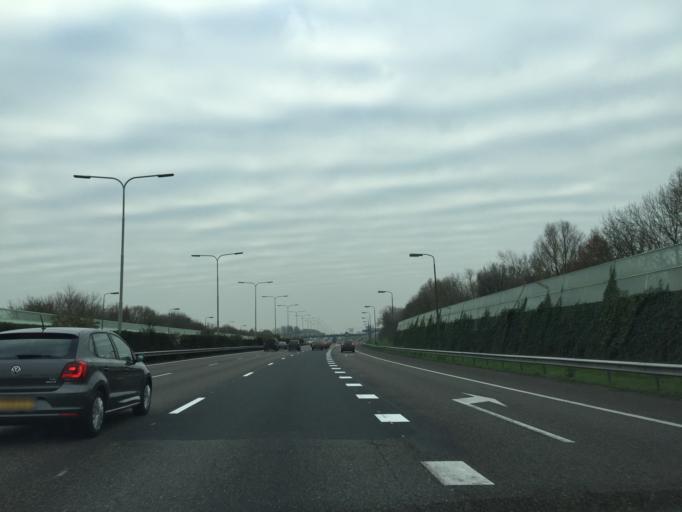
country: NL
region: South Holland
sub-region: Gemeente Delft
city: Delft
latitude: 52.0041
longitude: 4.3854
